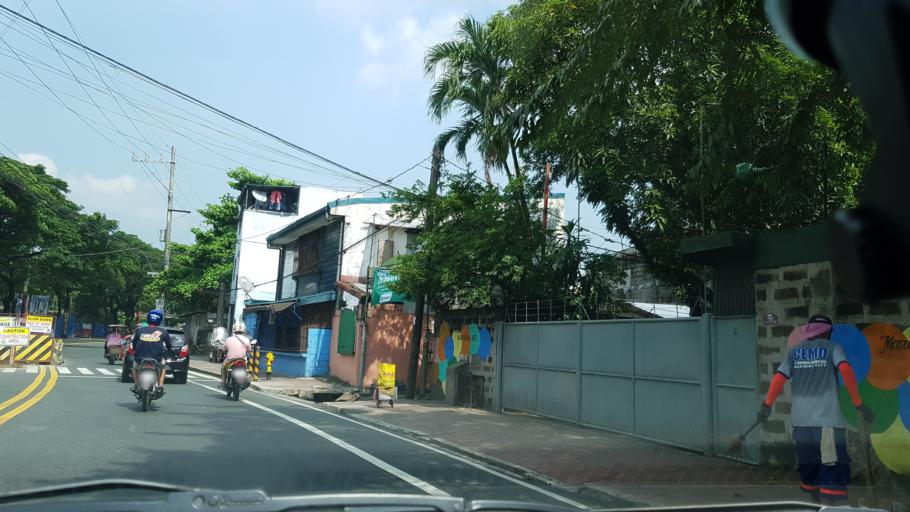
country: PH
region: Calabarzon
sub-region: Province of Rizal
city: San Mateo
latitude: 14.6625
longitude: 121.1206
